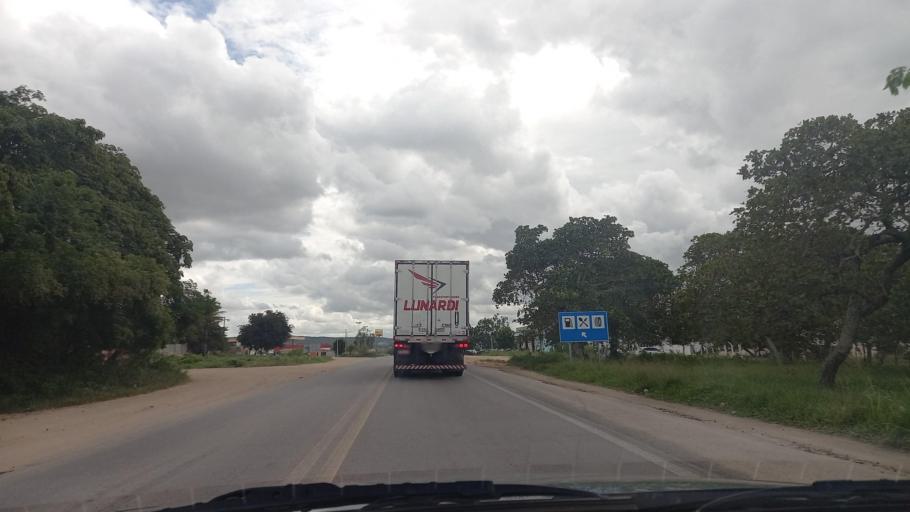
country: BR
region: Pernambuco
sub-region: Lajedo
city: Lajedo
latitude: -8.6605
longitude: -36.3396
